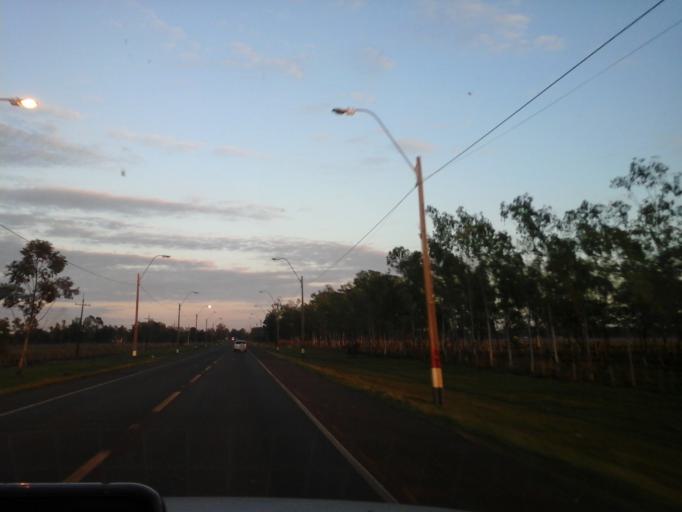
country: PY
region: Itapua
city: General Delgado
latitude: -27.0874
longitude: -56.5328
